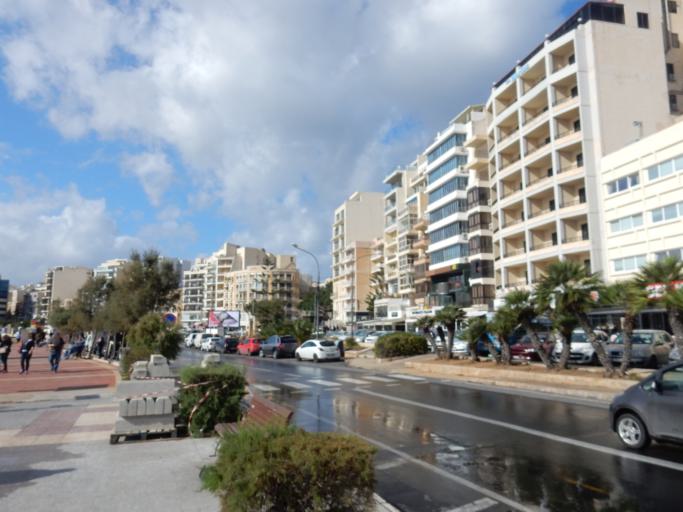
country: MT
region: Tas-Sliema
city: Sliema
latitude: 35.9080
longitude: 14.5065
